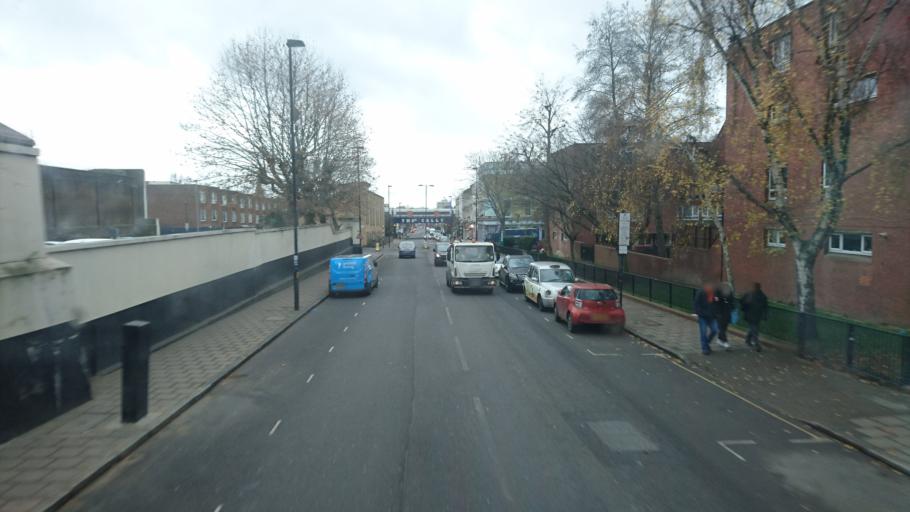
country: GB
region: England
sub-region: Greater London
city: Barnsbury
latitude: 51.5446
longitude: -0.1177
